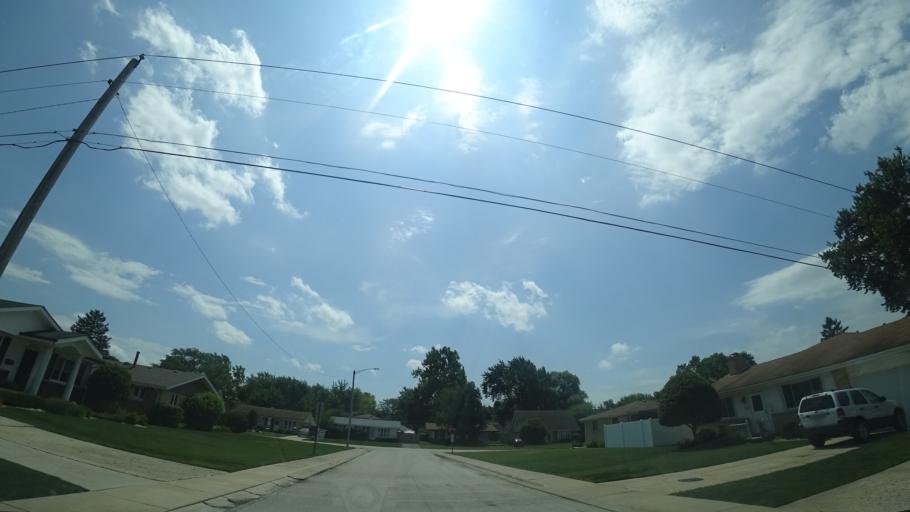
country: US
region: Illinois
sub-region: Cook County
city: Crestwood
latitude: 41.6579
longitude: -87.7516
